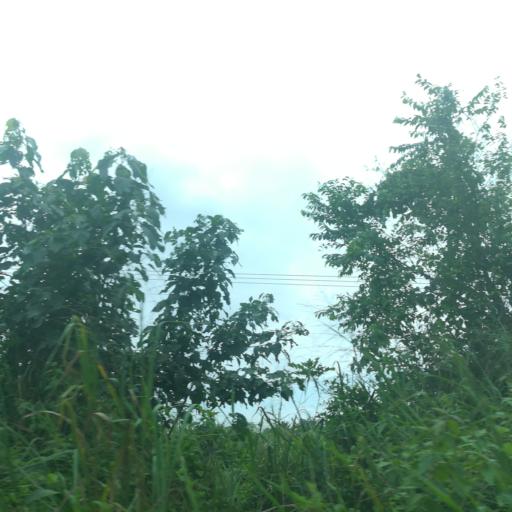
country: NG
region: Lagos
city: Ejirin
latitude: 6.6544
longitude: 3.7126
